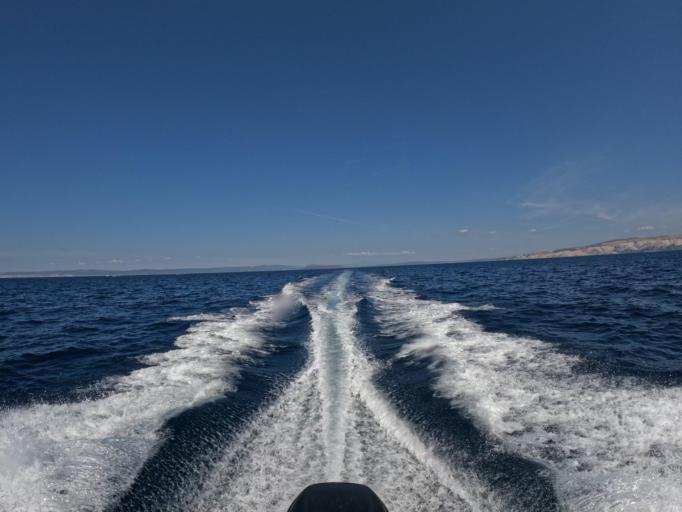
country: HR
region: Primorsko-Goranska
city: Lopar
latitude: 44.8820
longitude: 14.6558
